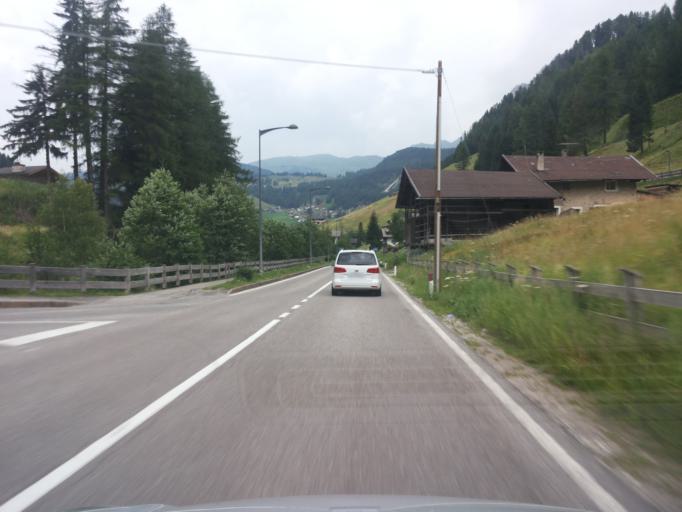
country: IT
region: Trentino-Alto Adige
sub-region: Bolzano
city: Selva
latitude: 46.5475
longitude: 11.7678
